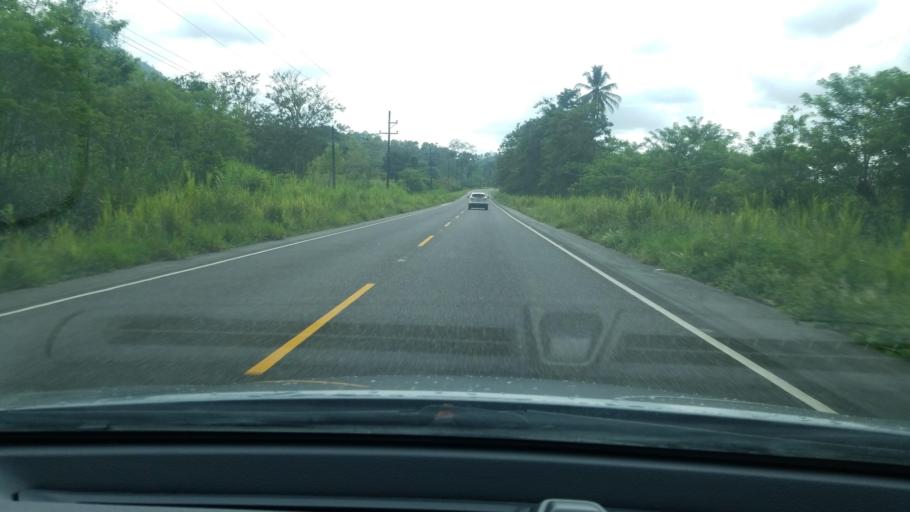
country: HN
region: Cortes
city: Potrerillos
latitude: 15.6134
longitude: -88.2803
